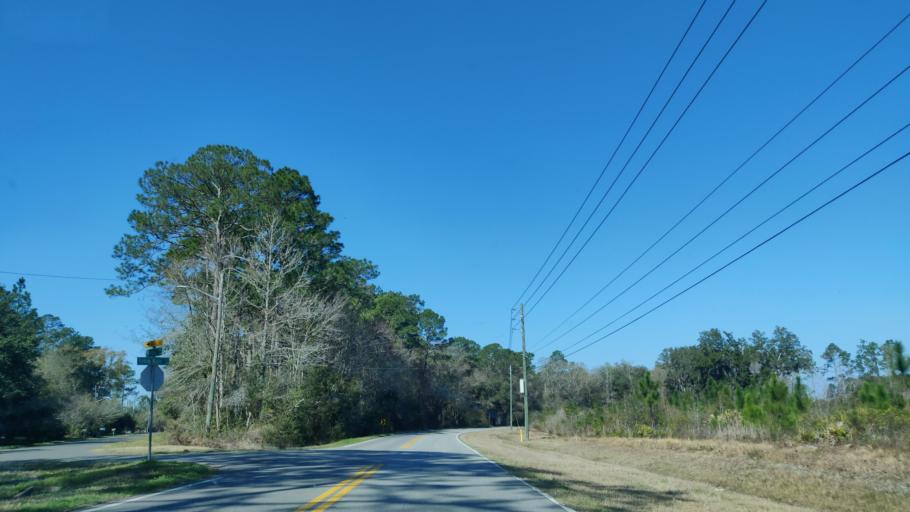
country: US
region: Florida
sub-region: Duval County
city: Baldwin
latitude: 30.2452
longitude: -81.9455
